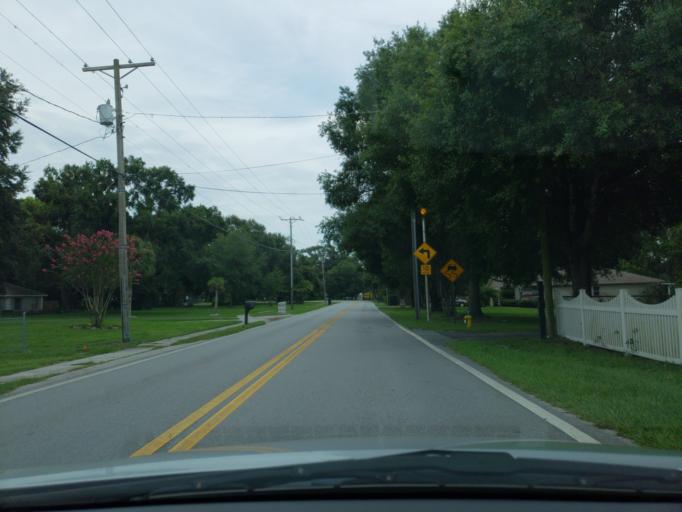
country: US
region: Florida
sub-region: Hillsborough County
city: Lutz
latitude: 28.1554
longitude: -82.4761
